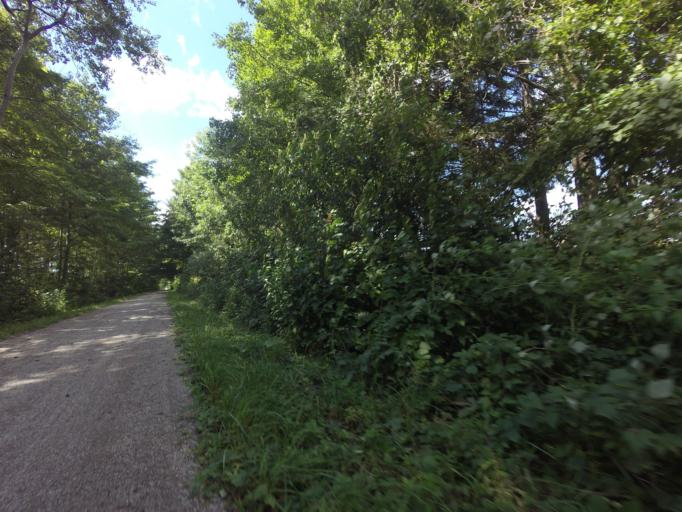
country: CA
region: Ontario
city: Huron East
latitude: 43.6671
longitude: -81.2678
